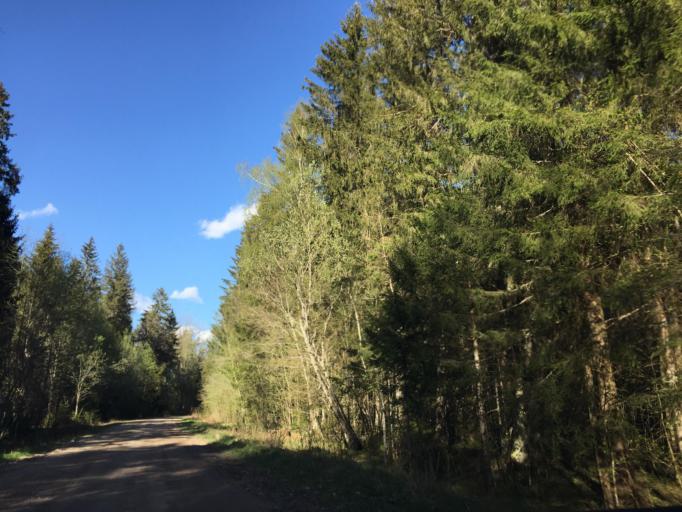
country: LV
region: Vecpiebalga
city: Vecpiebalga
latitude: 56.8641
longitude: 25.9676
